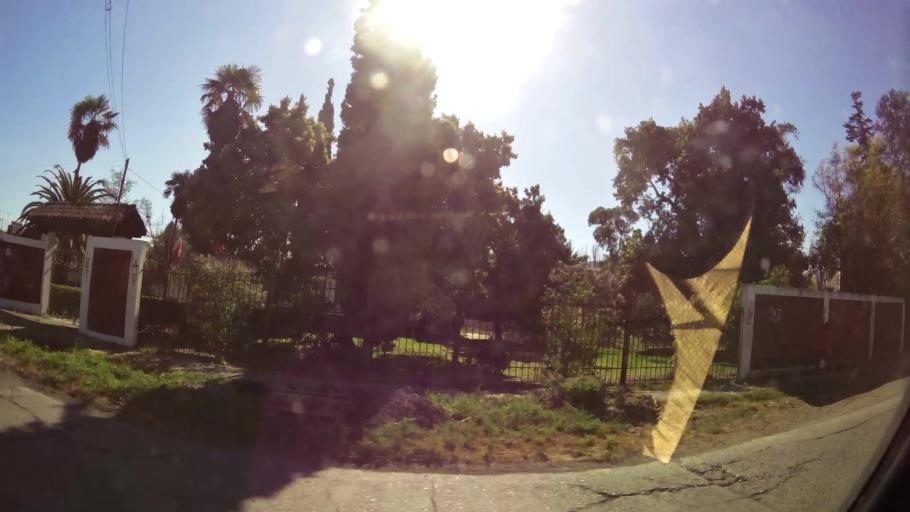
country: CL
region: Santiago Metropolitan
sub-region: Provincia de Talagante
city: Penaflor
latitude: -33.6035
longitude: -70.8979
